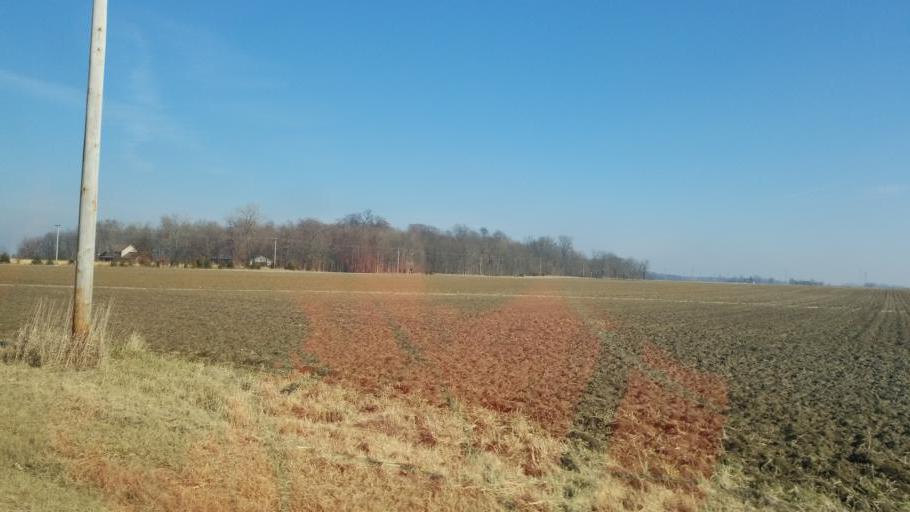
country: US
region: Ohio
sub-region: Seneca County
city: Tiffin
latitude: 41.0066
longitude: -83.0742
